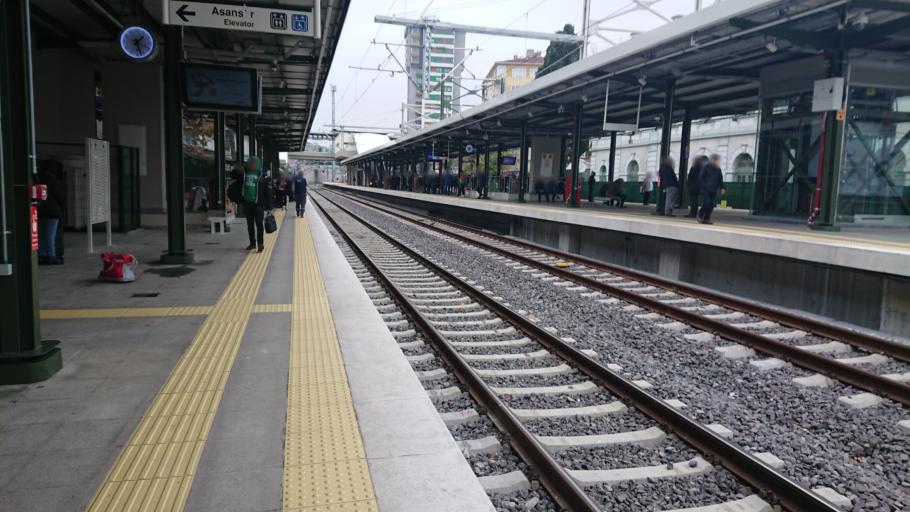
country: TR
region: Istanbul
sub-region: Atasehir
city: Atasehir
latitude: 40.9537
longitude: 29.0956
